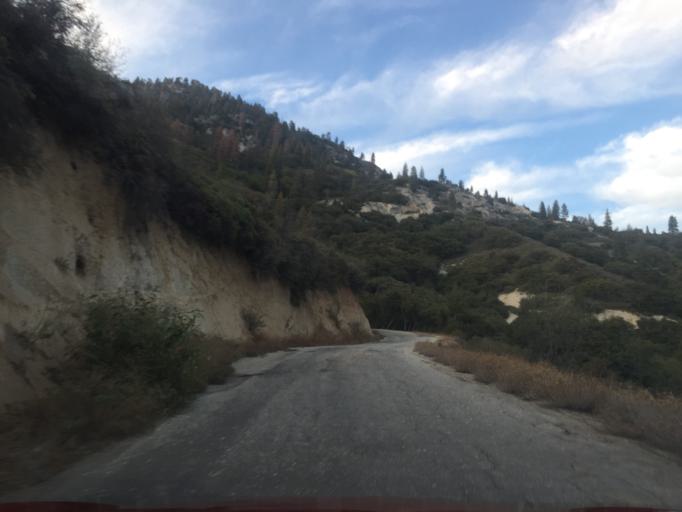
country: US
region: California
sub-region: Tulare County
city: Three Rivers
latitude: 36.4451
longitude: -118.7093
